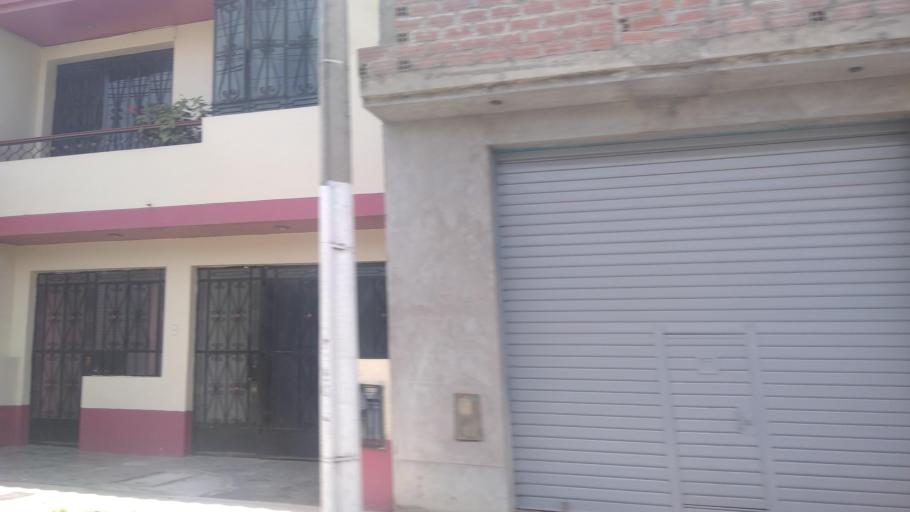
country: PE
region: Lima
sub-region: Lima
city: Independencia
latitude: -11.9672
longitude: -76.9900
